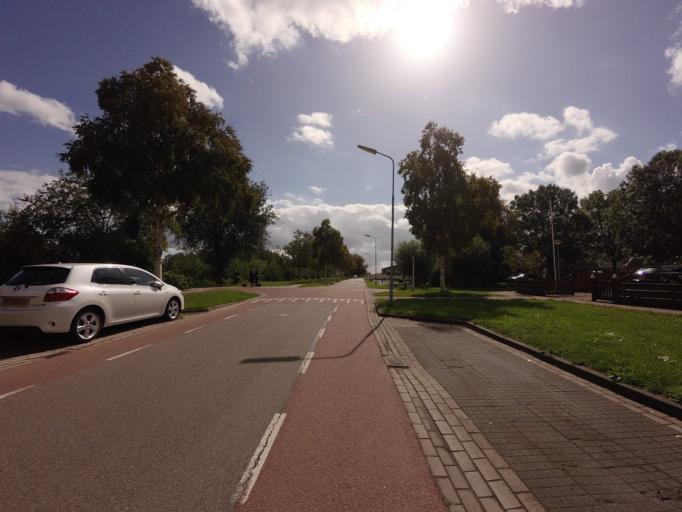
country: NL
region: North Holland
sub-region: Gemeente Purmerend
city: Purmerend
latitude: 52.5678
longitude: 4.9953
